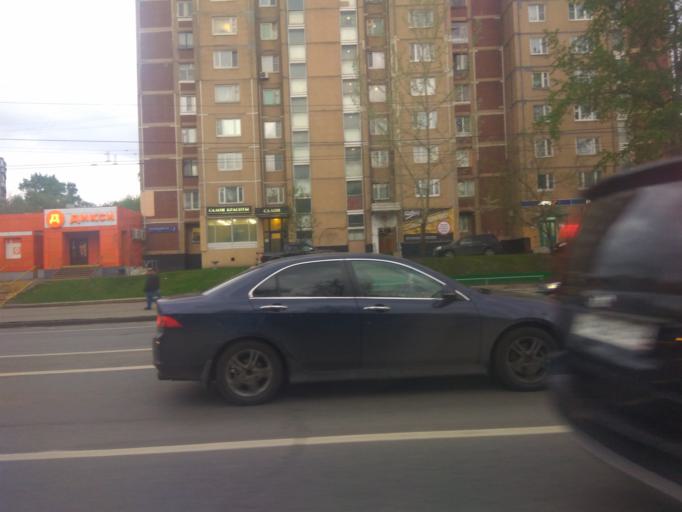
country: RU
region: Moskovskaya
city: Kuskovo
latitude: 55.7381
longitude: 37.8207
